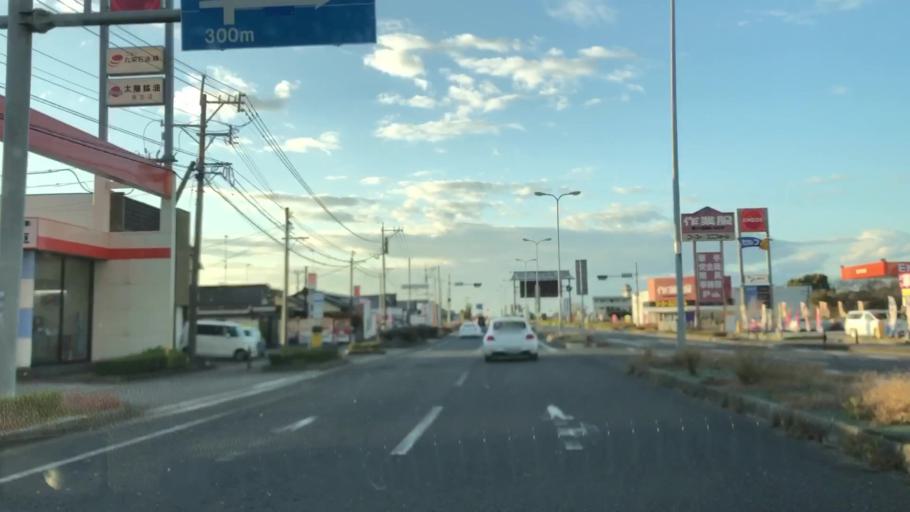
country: JP
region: Fukuoka
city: Nakatsu
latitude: 33.5395
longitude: 131.2943
